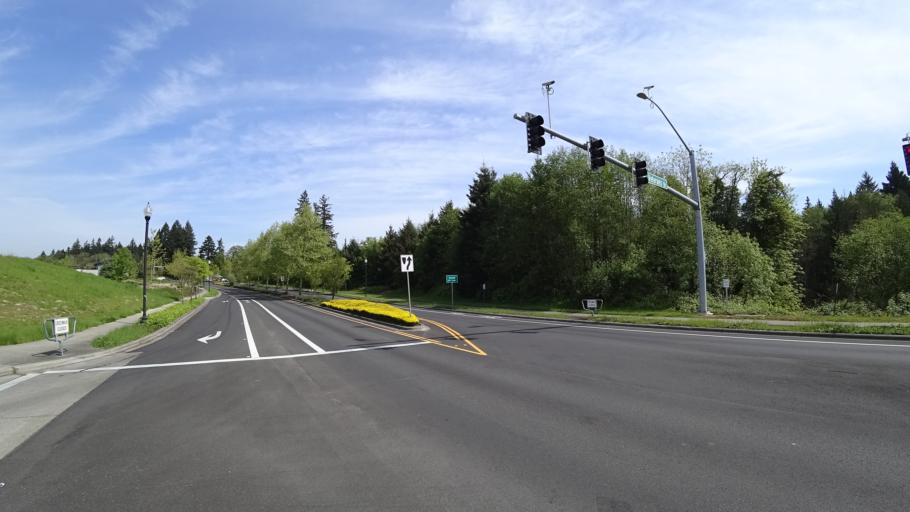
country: US
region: Oregon
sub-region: Washington County
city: Hillsboro
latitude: 45.5309
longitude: -122.9377
